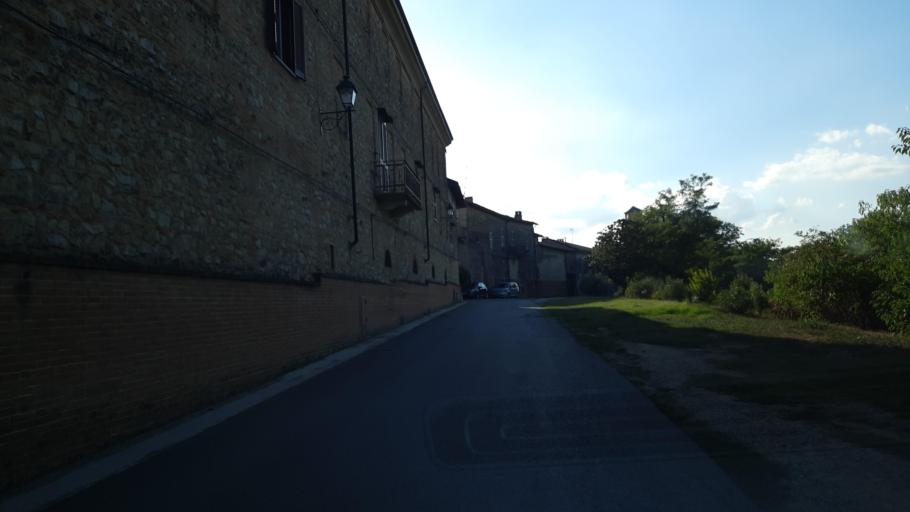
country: IT
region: Piedmont
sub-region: Provincia di Asti
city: Grazzano Badoglio
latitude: 45.0387
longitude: 8.3179
